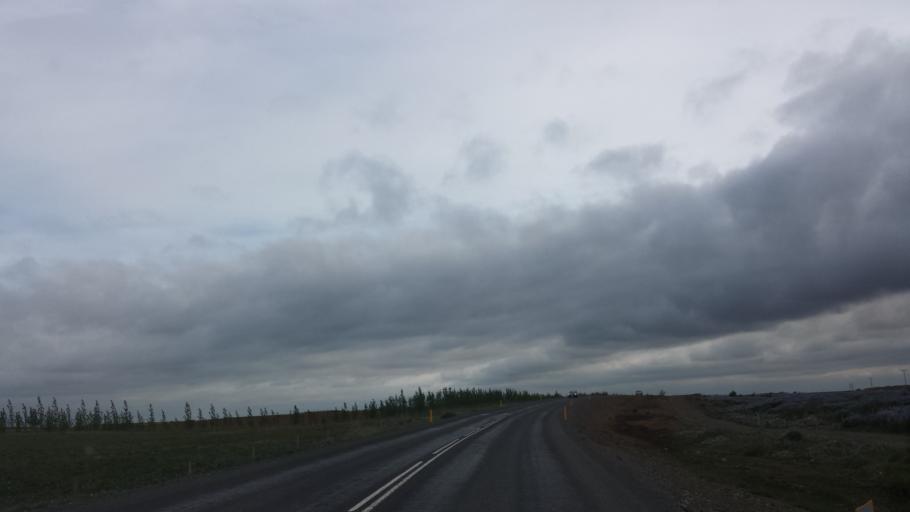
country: IS
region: South
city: Selfoss
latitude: 64.2777
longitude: -20.3489
